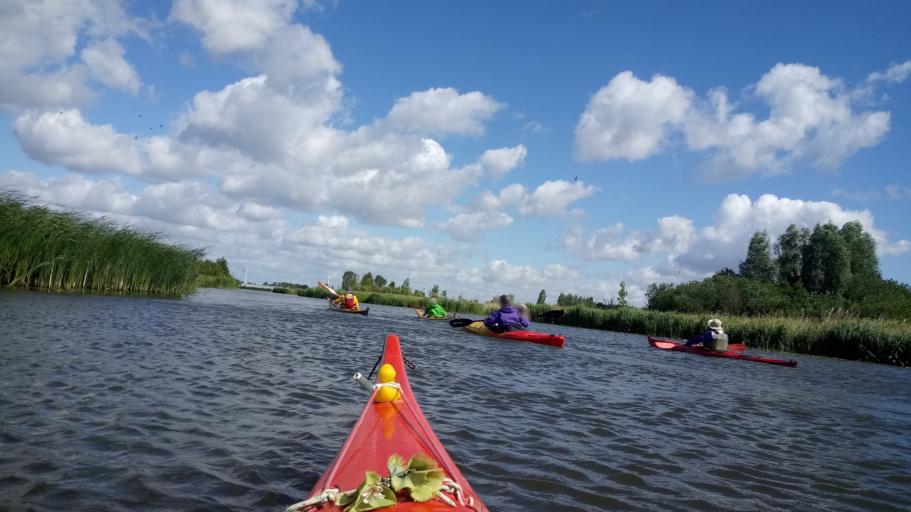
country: NL
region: North Holland
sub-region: Gemeente Enkhuizen
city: Enkhuizen
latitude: 52.7086
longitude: 5.1959
